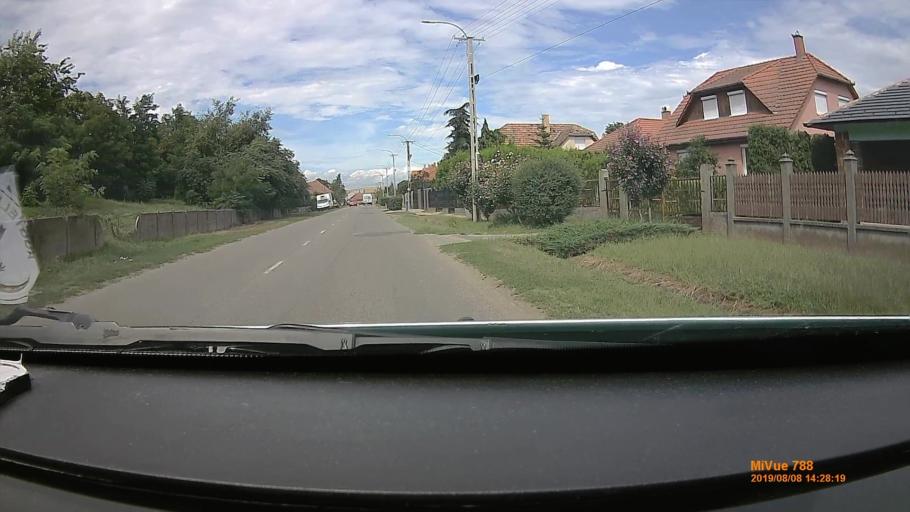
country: HU
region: Szabolcs-Szatmar-Bereg
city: Mateszalka
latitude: 47.9486
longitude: 22.3216
